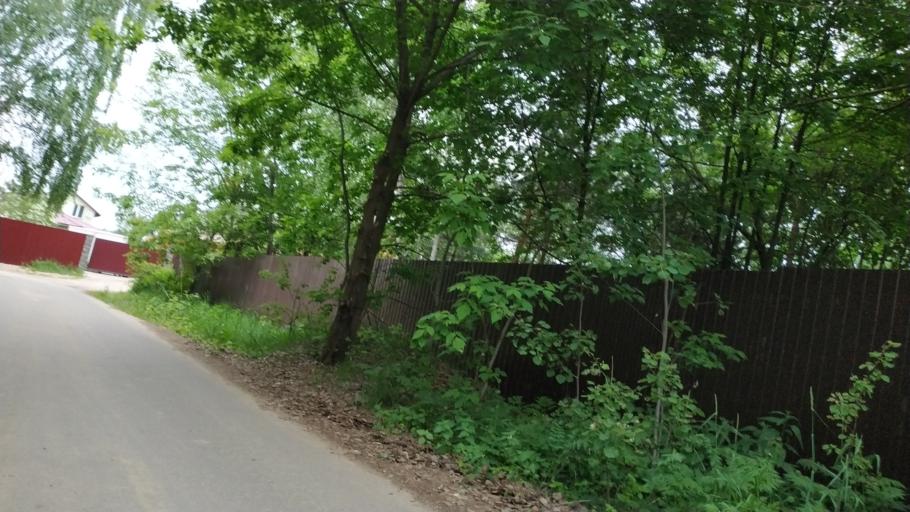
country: RU
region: Moskovskaya
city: Ostrovtsy
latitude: 55.5215
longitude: 37.9967
